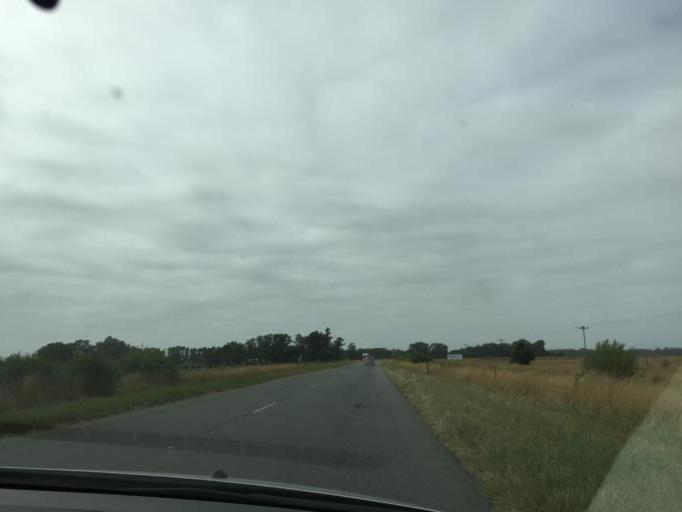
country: AR
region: Buenos Aires
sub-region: Partido de Las Flores
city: Las Flores
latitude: -36.2027
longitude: -59.0508
